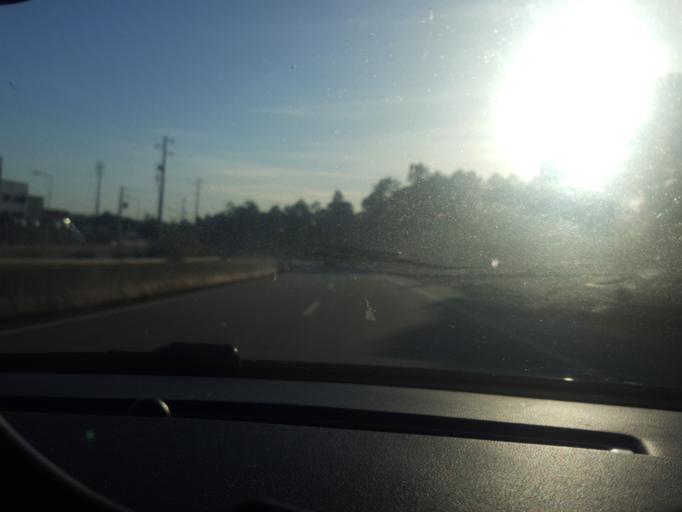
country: PT
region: Viseu
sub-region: Concelho de Carregal do Sal
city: Carregal do Sal
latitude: 40.4615
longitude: -7.9635
